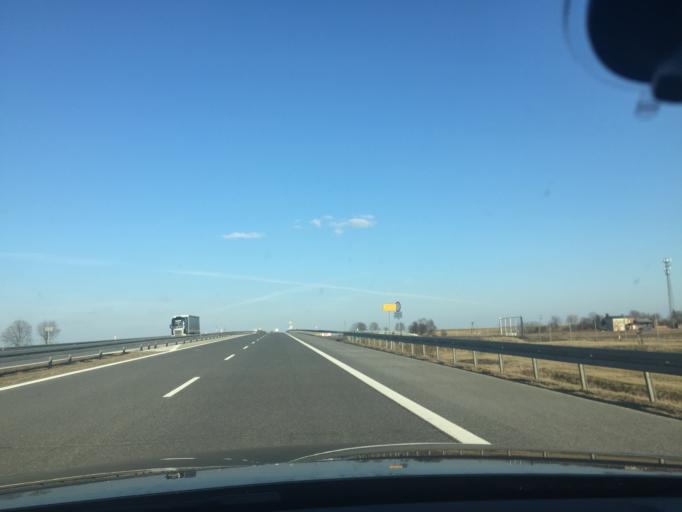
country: PL
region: Lubusz
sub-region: Powiat swiebodzinski
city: Zbaszynek
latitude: 52.3073
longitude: 15.7640
